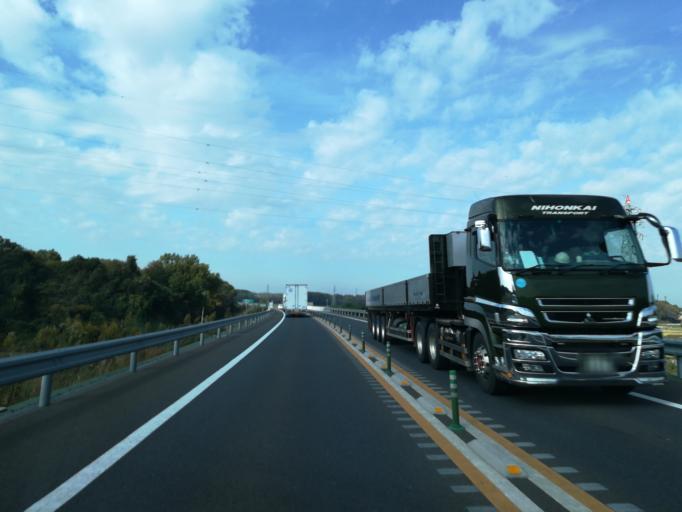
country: JP
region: Ibaraki
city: Iwai
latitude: 36.0792
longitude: 139.9155
